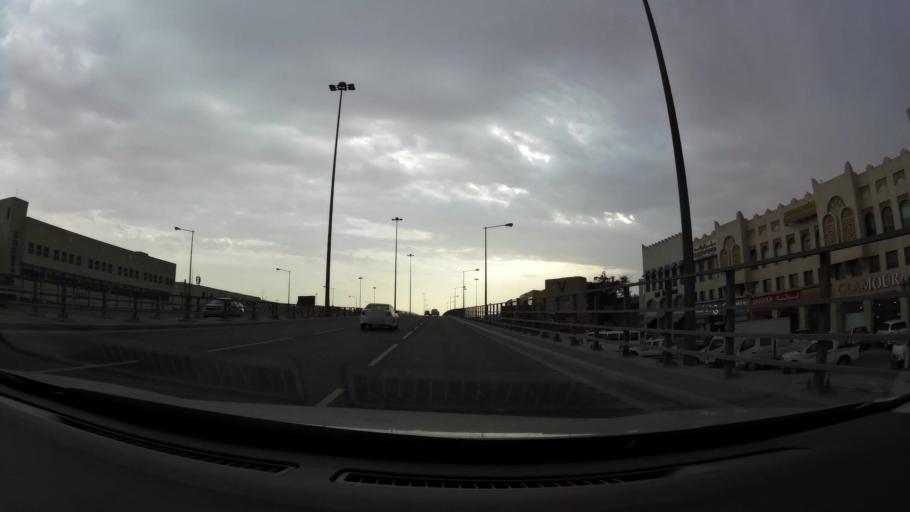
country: QA
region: Baladiyat ad Dawhah
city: Doha
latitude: 25.2655
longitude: 51.4993
